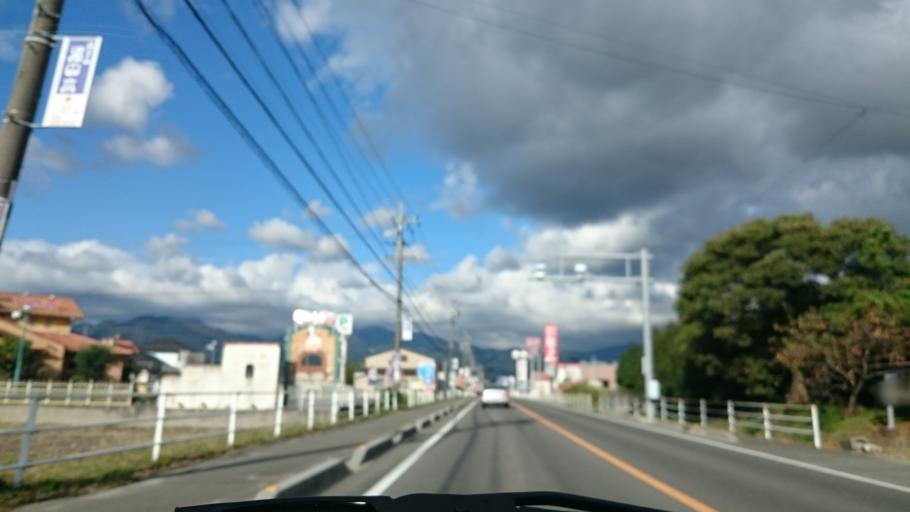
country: JP
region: Mie
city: Komono
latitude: 35.0006
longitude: 136.5378
